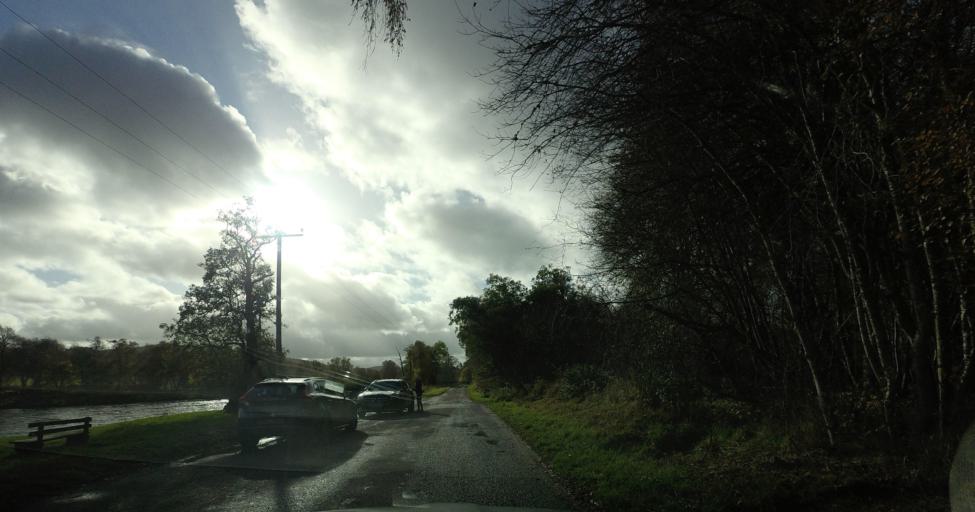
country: GB
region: Scotland
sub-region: Highland
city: Grantown on Spey
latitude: 57.3196
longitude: -3.6144
